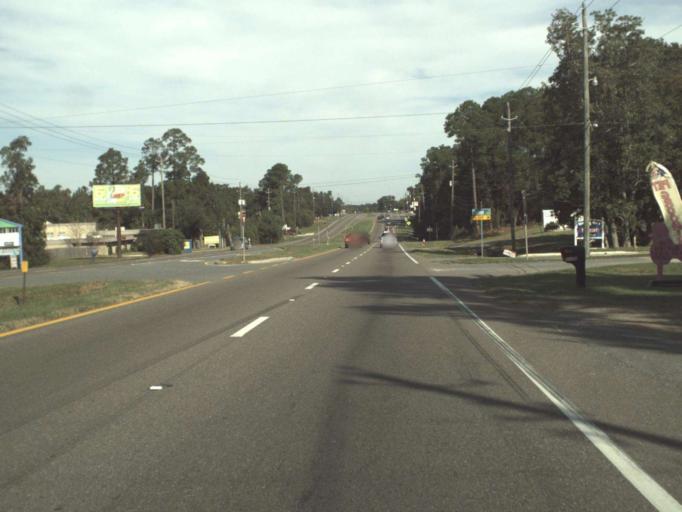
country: US
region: Florida
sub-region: Escambia County
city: Bellview
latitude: 30.4957
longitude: -87.3059
